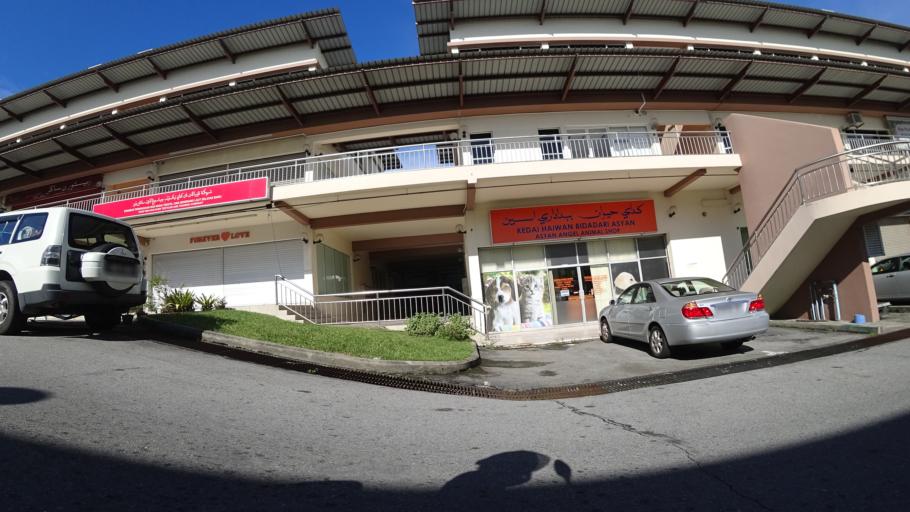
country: BN
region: Brunei and Muara
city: Bandar Seri Begawan
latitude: 4.9498
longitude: 114.9670
